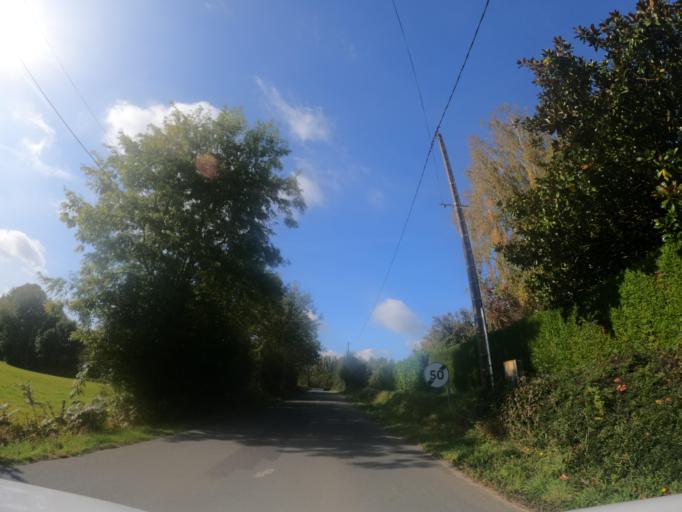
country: FR
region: Poitou-Charentes
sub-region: Departement des Deux-Sevres
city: Courlay
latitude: 46.7849
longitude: -0.5920
